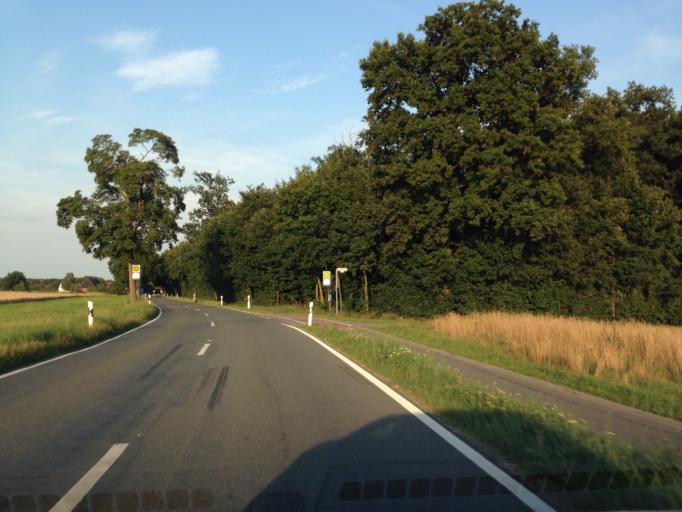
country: DE
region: North Rhine-Westphalia
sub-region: Regierungsbezirk Munster
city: Senden
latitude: 51.8242
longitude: 7.5217
